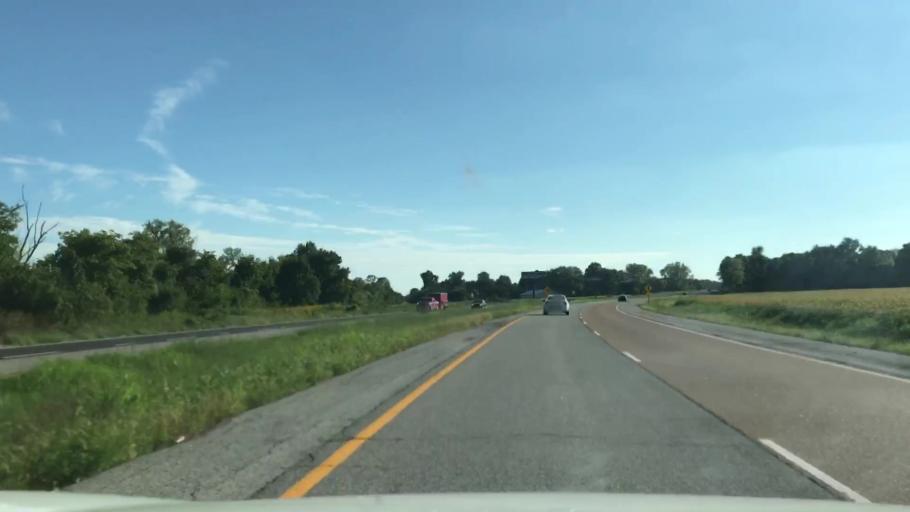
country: US
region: Illinois
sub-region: Madison County
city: Mitchell
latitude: 38.7821
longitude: -90.1089
